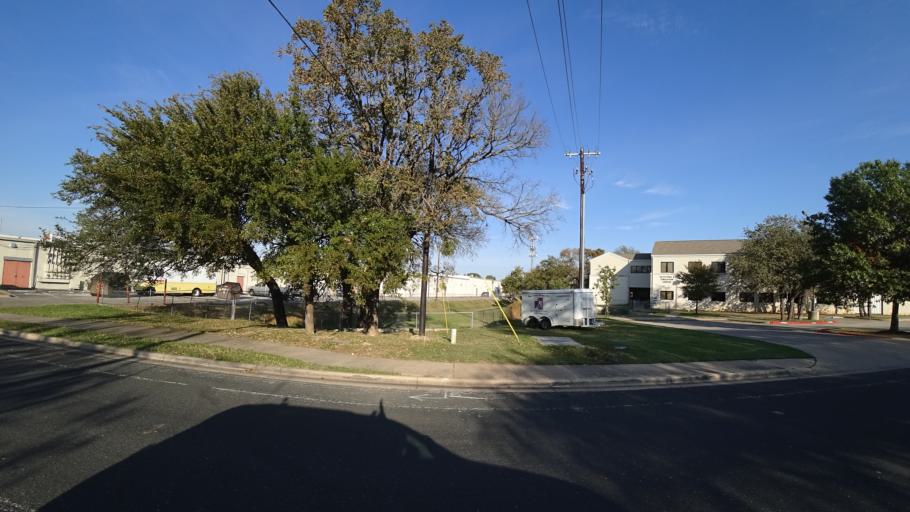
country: US
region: Texas
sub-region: Williamson County
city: Anderson Mill
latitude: 30.4460
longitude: -97.8071
